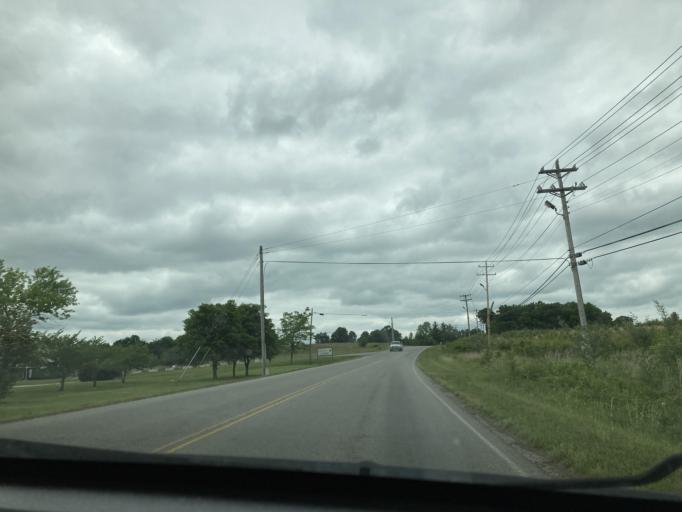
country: US
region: Tennessee
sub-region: Dickson County
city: Burns
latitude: 36.0490
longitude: -87.3440
